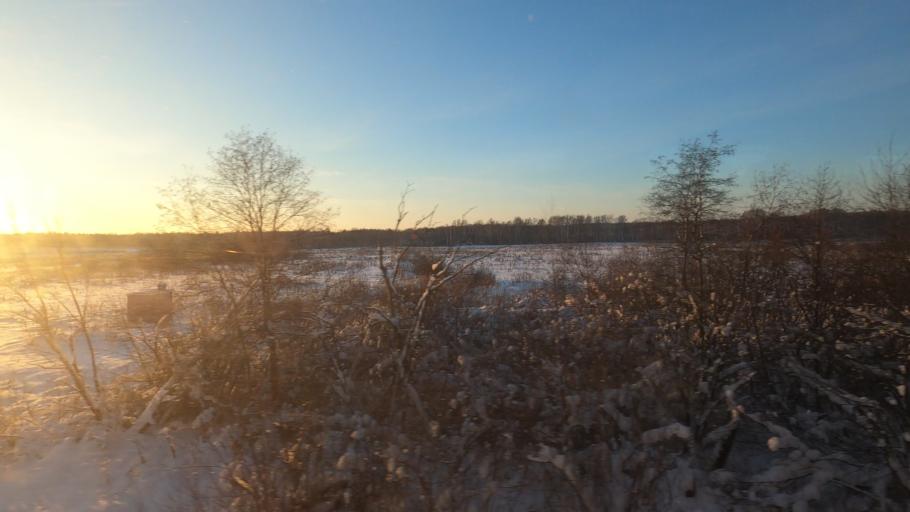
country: RU
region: Moskovskaya
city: Orud'yevo
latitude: 56.4159
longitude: 37.4970
